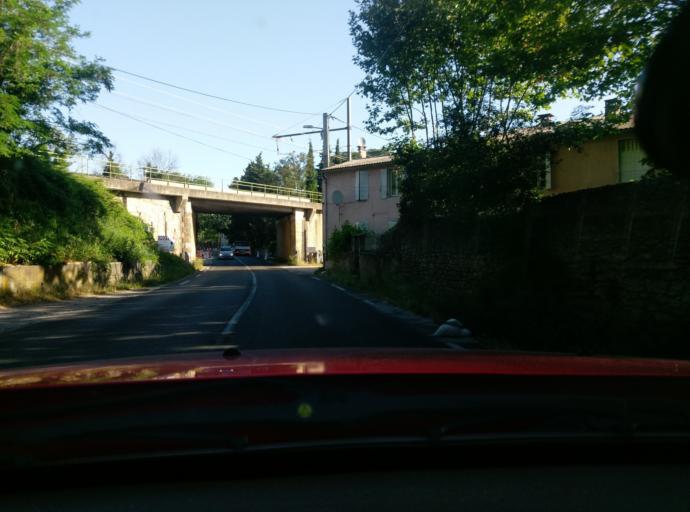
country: FR
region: Languedoc-Roussillon
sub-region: Departement du Gard
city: Remoulins
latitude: 43.9323
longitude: 4.5598
